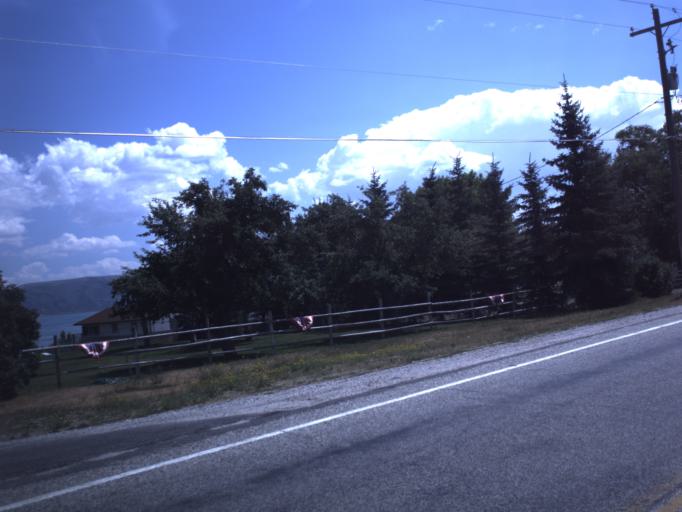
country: US
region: Idaho
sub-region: Bear Lake County
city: Paris
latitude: 41.9521
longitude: -111.3934
